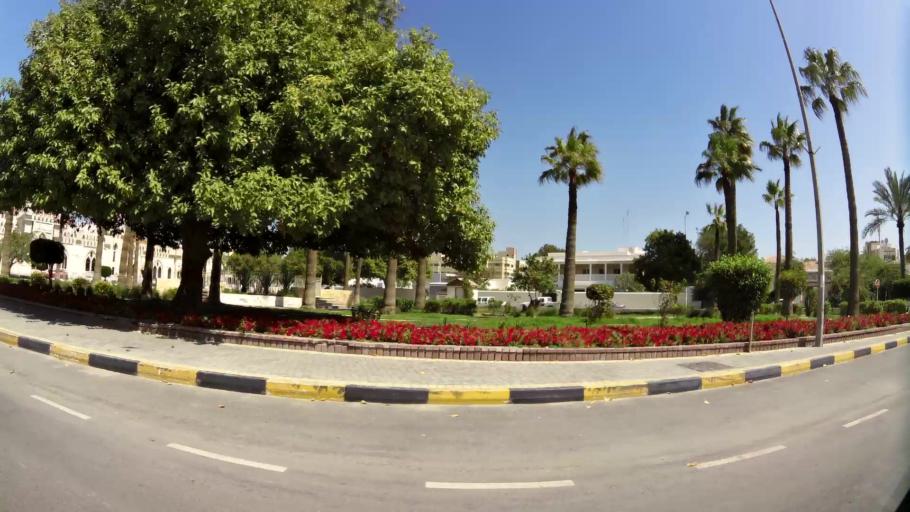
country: BH
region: Manama
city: Manama
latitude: 26.2230
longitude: 50.5883
